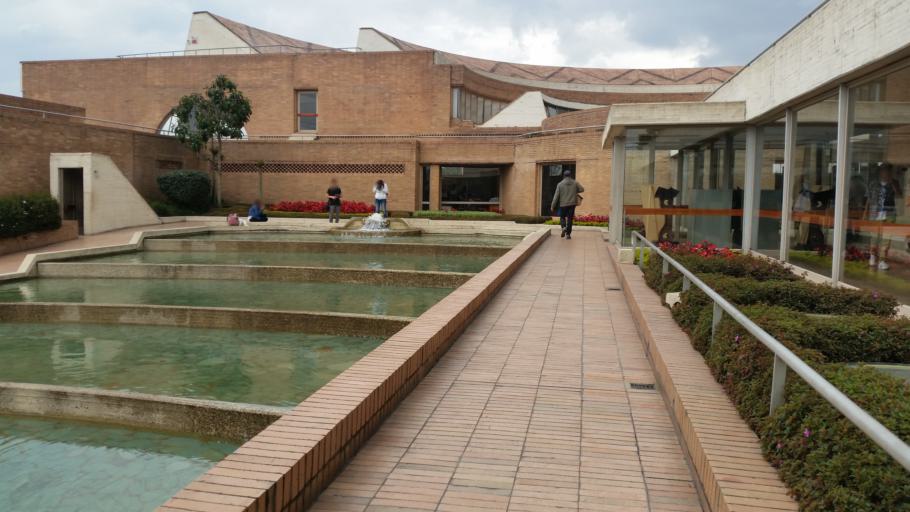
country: CO
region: Bogota D.C.
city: Bogota
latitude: 4.6569
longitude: -74.0888
